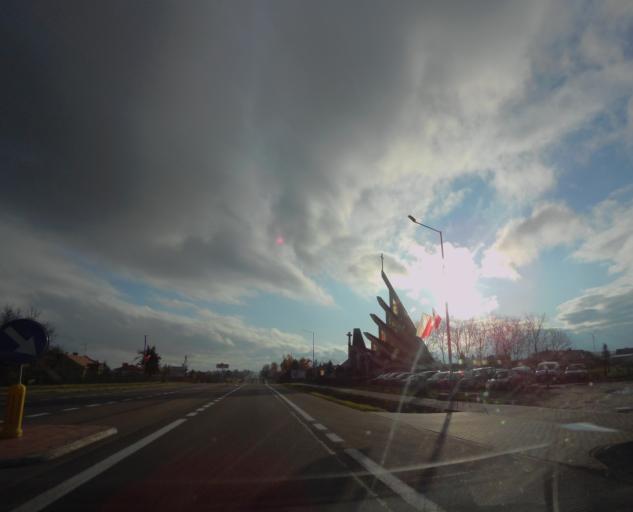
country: PL
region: Subcarpathian Voivodeship
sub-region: Powiat przemyski
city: Orly
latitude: 49.8728
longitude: 22.8115
